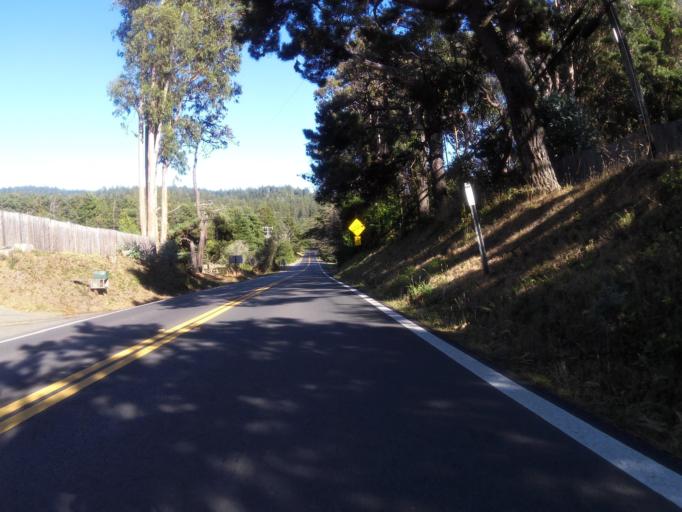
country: US
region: California
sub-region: Sonoma County
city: Sea Ranch
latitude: 38.8034
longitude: -123.5855
